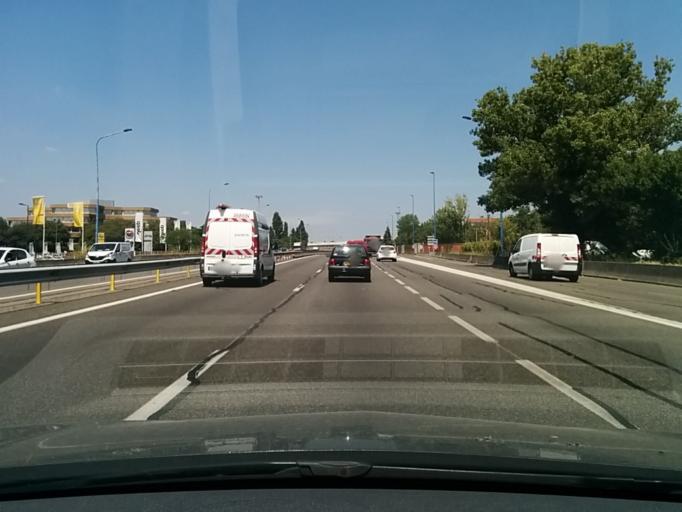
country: FR
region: Midi-Pyrenees
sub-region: Departement de la Haute-Garonne
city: Toulouse
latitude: 43.5735
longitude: 1.4099
